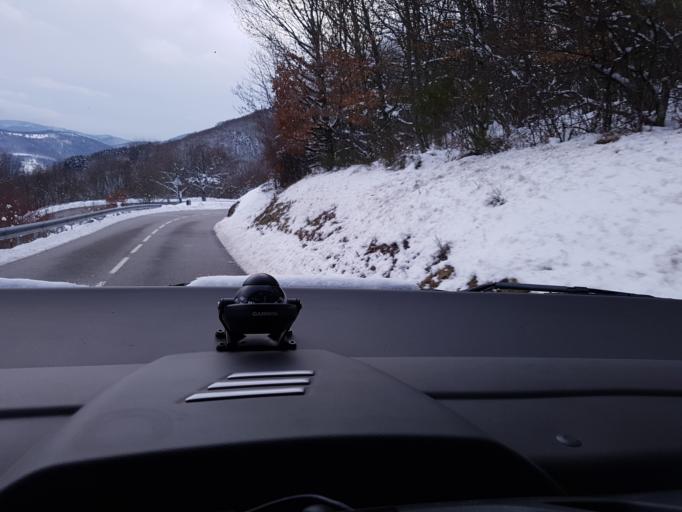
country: FR
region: Alsace
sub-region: Departement du Bas-Rhin
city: Ville
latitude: 48.3695
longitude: 7.2809
